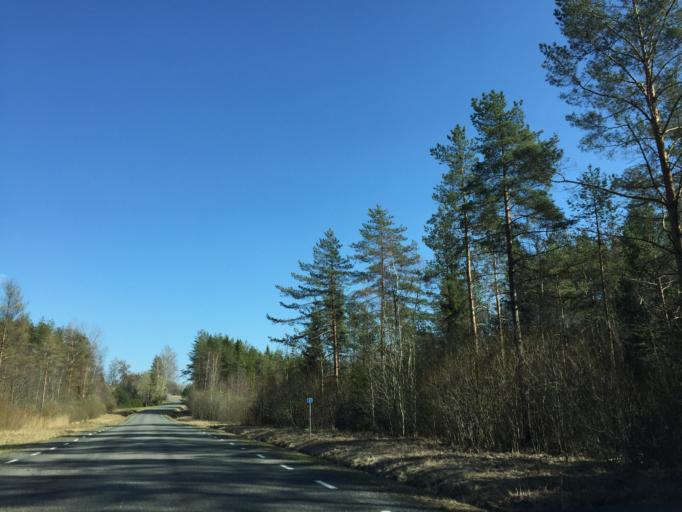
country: EE
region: Viljandimaa
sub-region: Viiratsi vald
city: Viiratsi
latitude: 58.2692
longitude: 25.6493
